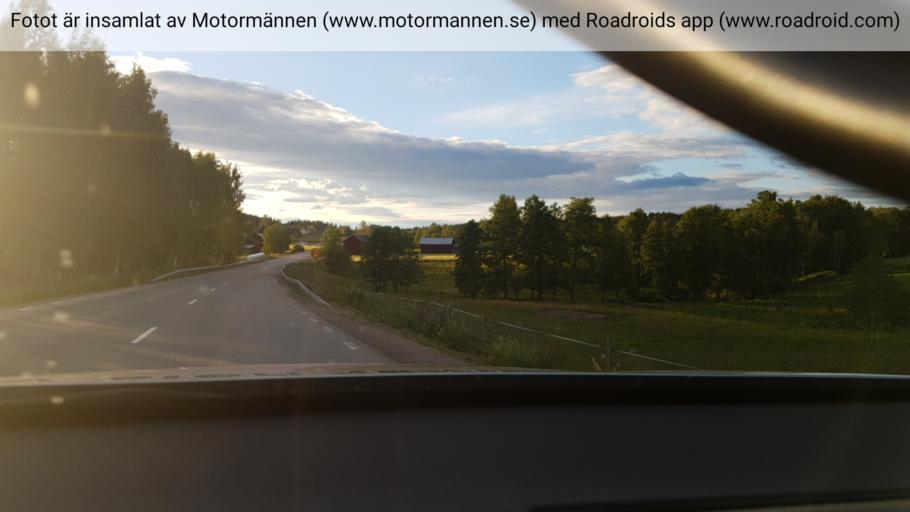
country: SE
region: Vaermland
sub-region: Torsby Kommun
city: Torsby
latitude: 60.0241
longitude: 13.1348
